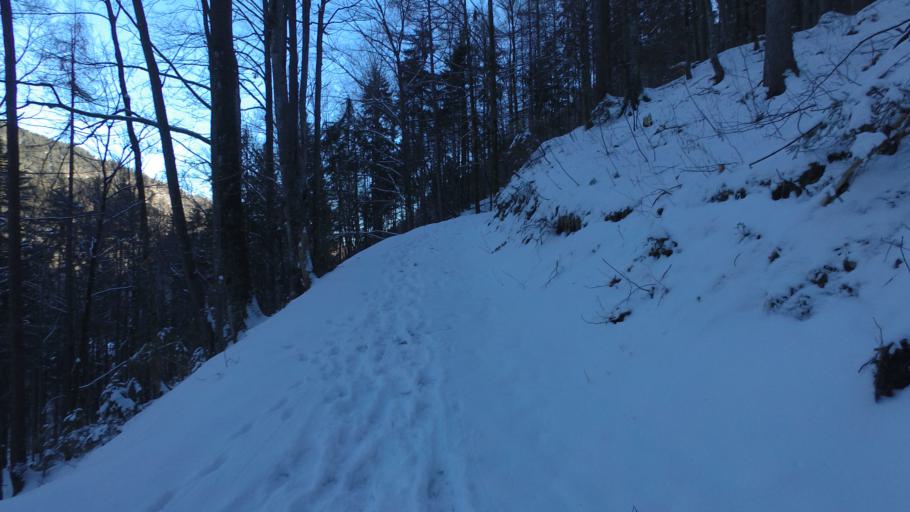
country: DE
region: Bavaria
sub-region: Upper Bavaria
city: Bergen
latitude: 47.7198
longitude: 12.5705
